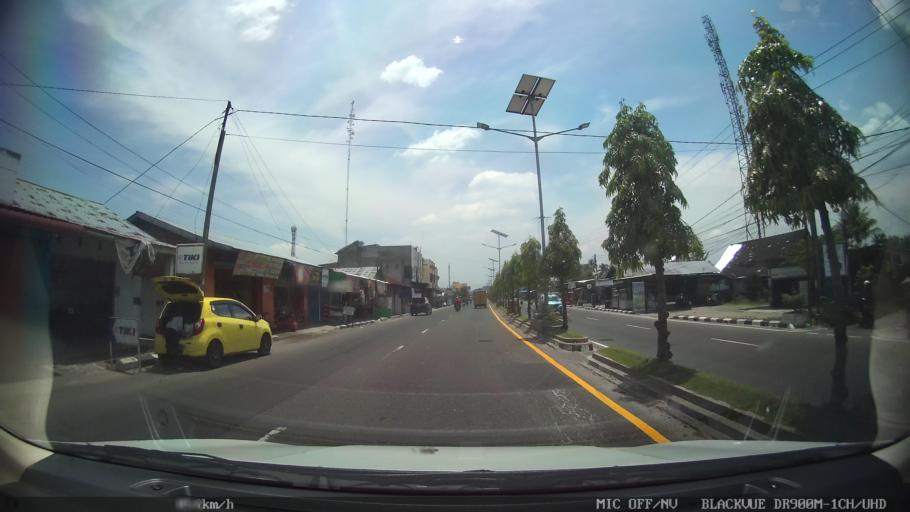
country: ID
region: North Sumatra
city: Binjai
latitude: 3.6088
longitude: 98.5136
